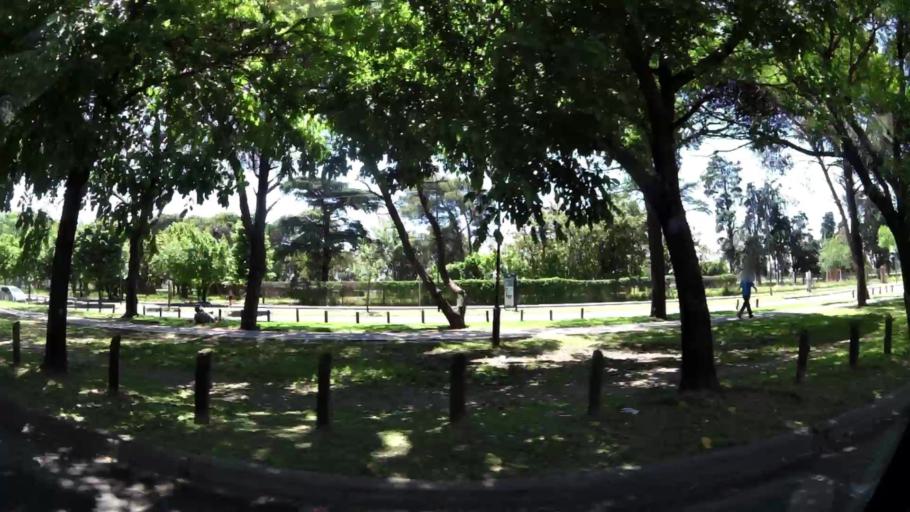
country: AR
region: Buenos Aires
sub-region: Partido de San Isidro
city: San Isidro
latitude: -34.4867
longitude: -58.5187
